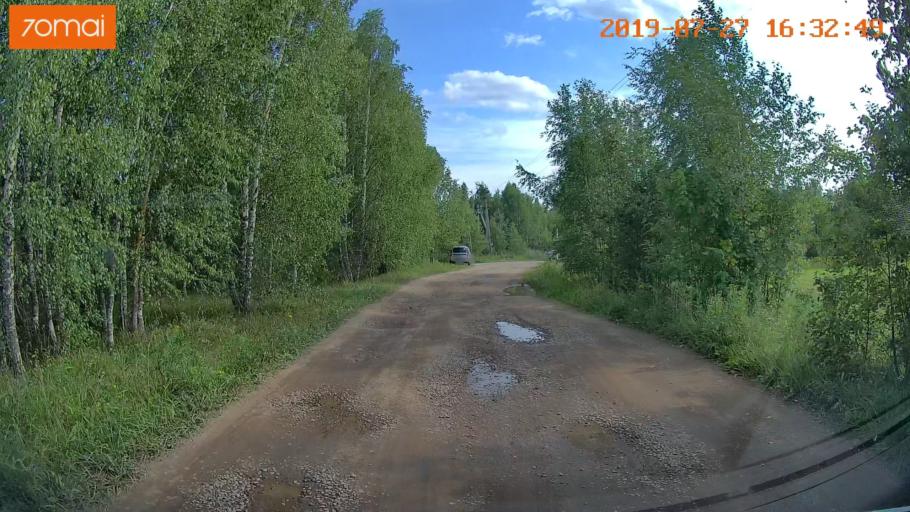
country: RU
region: Ivanovo
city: Novo-Talitsy
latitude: 57.0891
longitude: 40.8515
